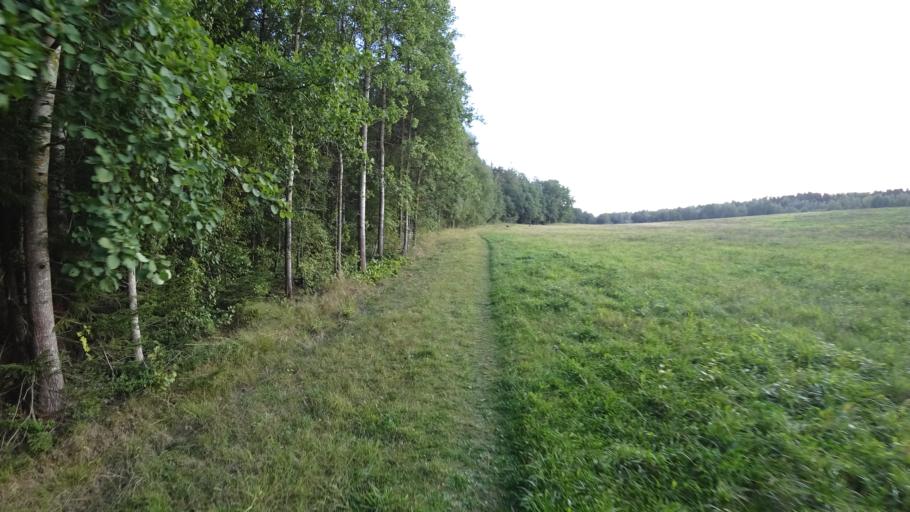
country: FI
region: Uusimaa
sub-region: Helsinki
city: Teekkarikylae
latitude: 60.2729
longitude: 24.8692
